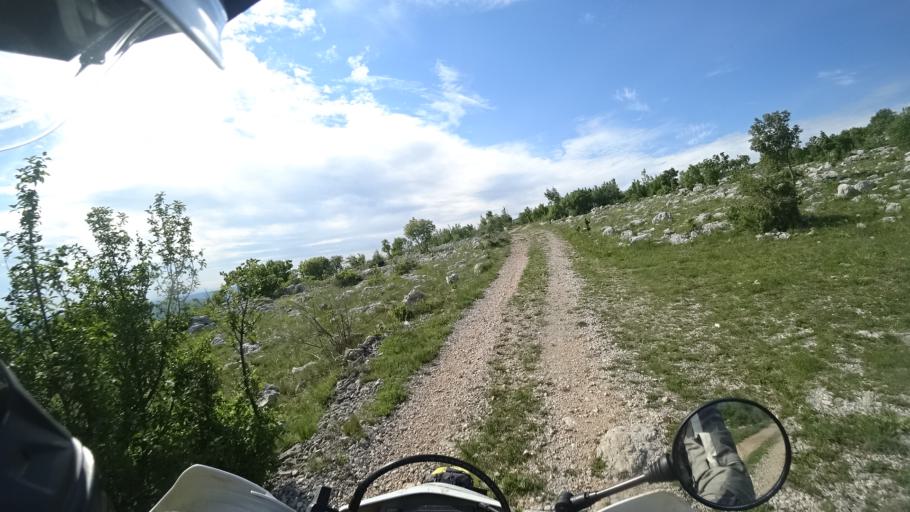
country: HR
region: Splitsko-Dalmatinska
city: Hrvace
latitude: 43.7849
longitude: 16.4370
